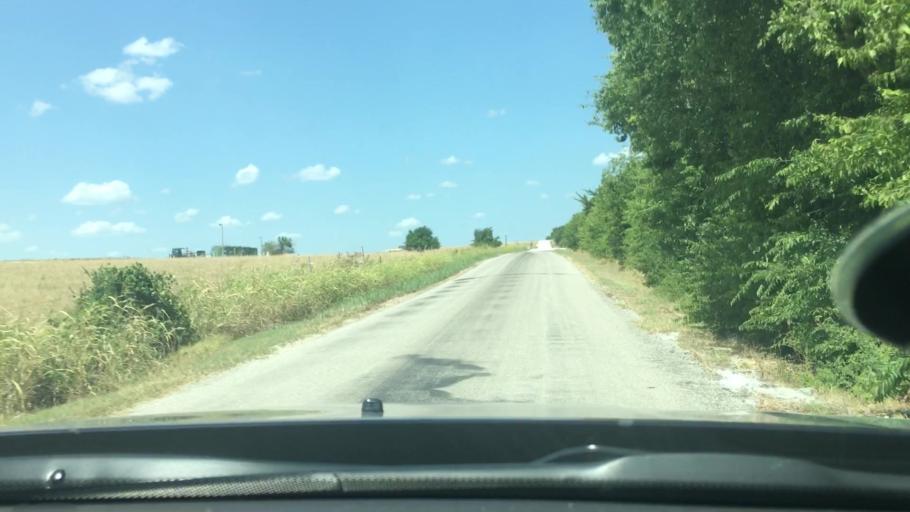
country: US
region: Oklahoma
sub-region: Love County
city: Marietta
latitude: 34.0021
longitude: -97.1914
